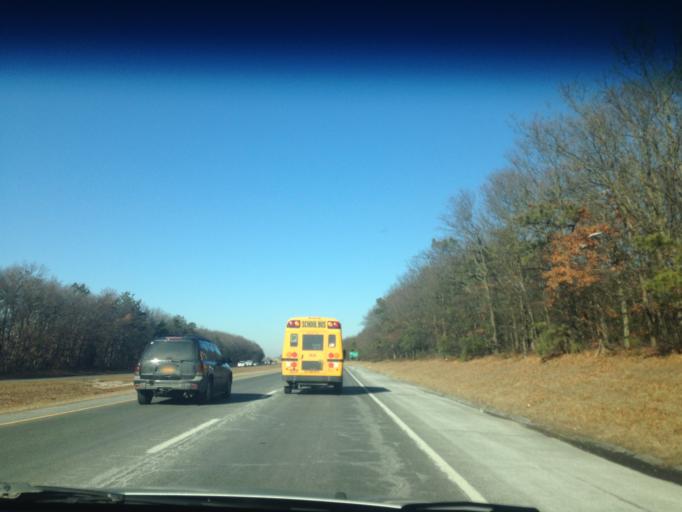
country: US
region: New York
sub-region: Suffolk County
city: Holtsville
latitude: 40.8002
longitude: -73.0513
